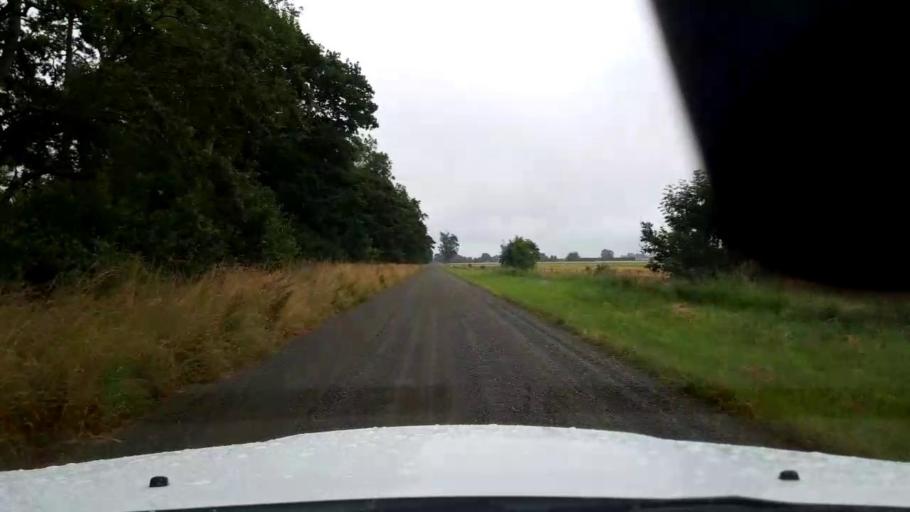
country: NZ
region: Canterbury
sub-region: Timaru District
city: Pleasant Point
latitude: -44.2095
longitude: 171.2814
